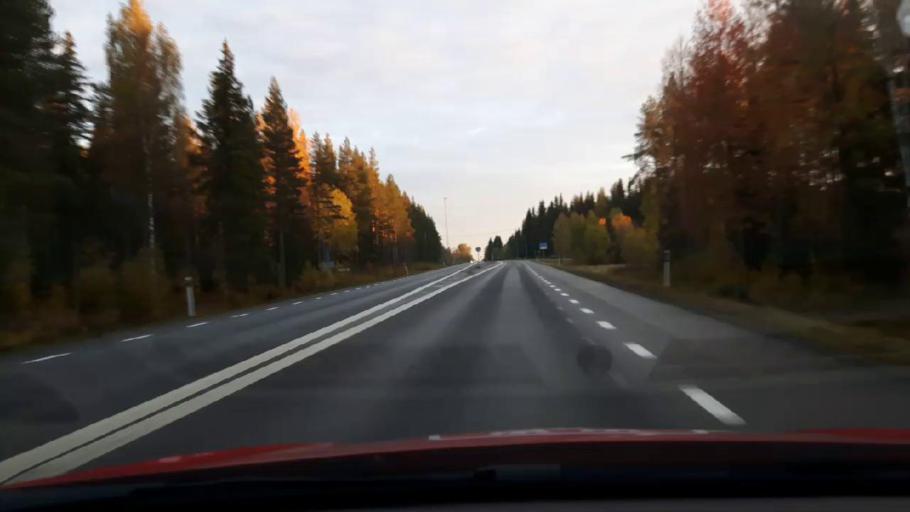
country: SE
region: Jaemtland
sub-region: OEstersunds Kommun
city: Lit
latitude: 63.2997
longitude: 14.8691
